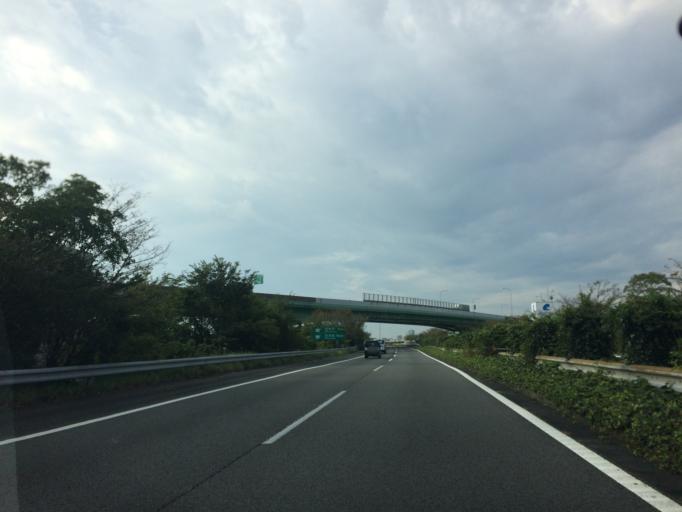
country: JP
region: Shizuoka
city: Shizuoka-shi
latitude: 35.0156
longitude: 138.4376
